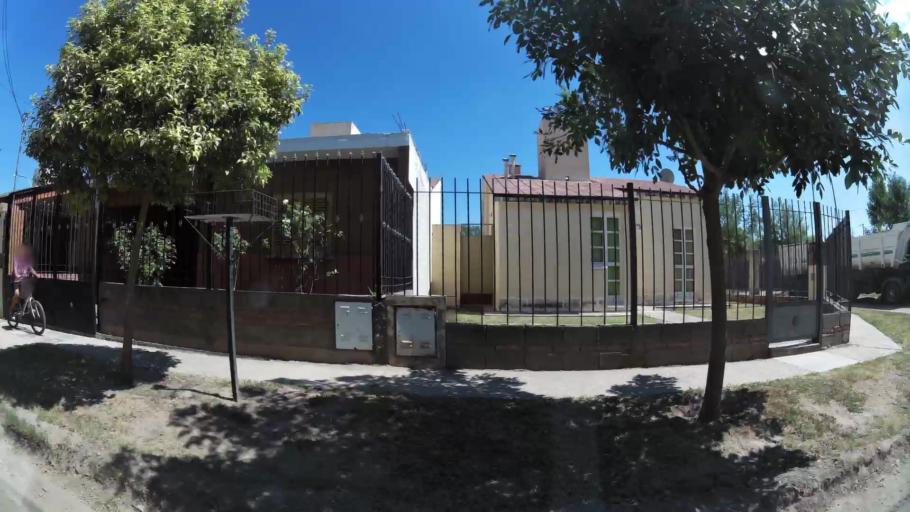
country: AR
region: Cordoba
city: Villa Allende
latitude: -31.3418
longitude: -64.2278
